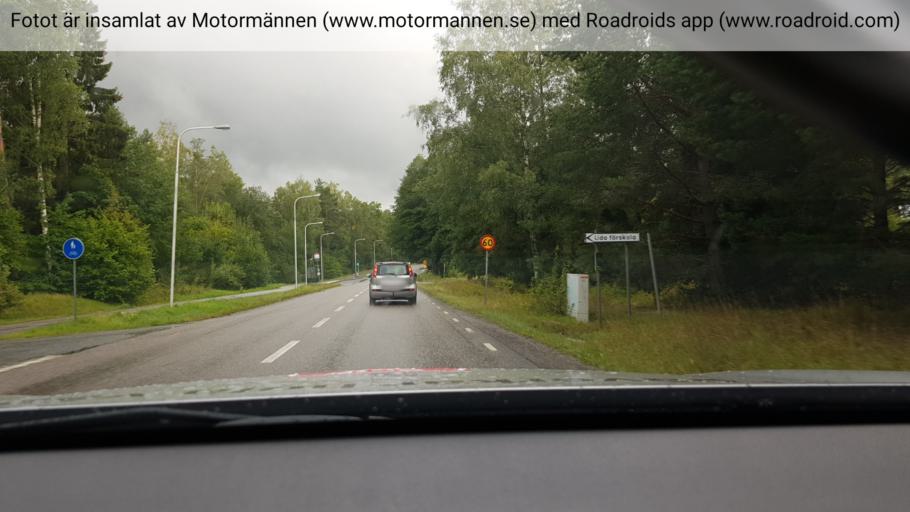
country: SE
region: Stockholm
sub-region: Haninge Kommun
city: Jordbro
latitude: 59.1160
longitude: 18.0614
